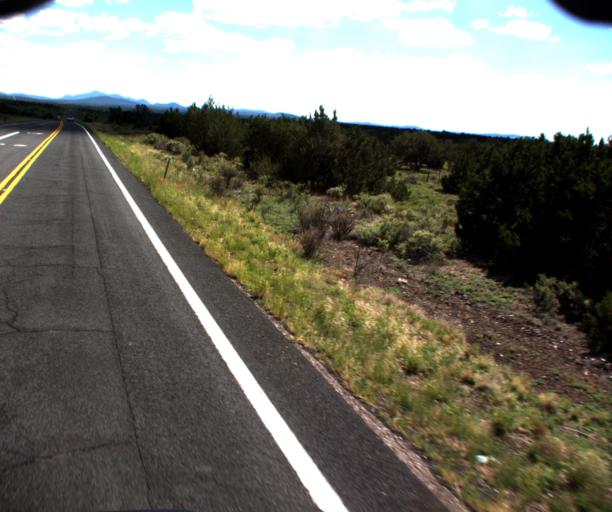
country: US
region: Arizona
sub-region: Coconino County
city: Williams
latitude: 35.5023
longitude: -112.1739
